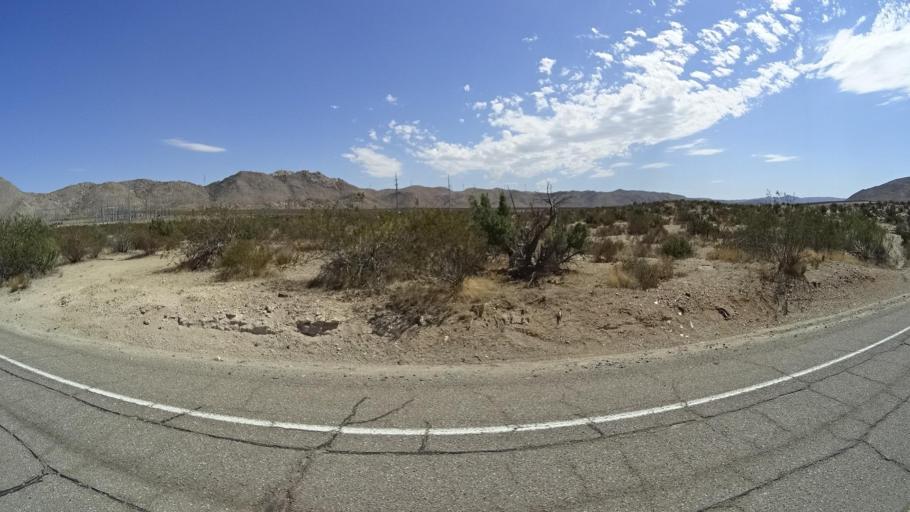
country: MX
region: Baja California
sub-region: Tecate
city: Cereso del Hongo
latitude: 32.6285
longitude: -116.1298
